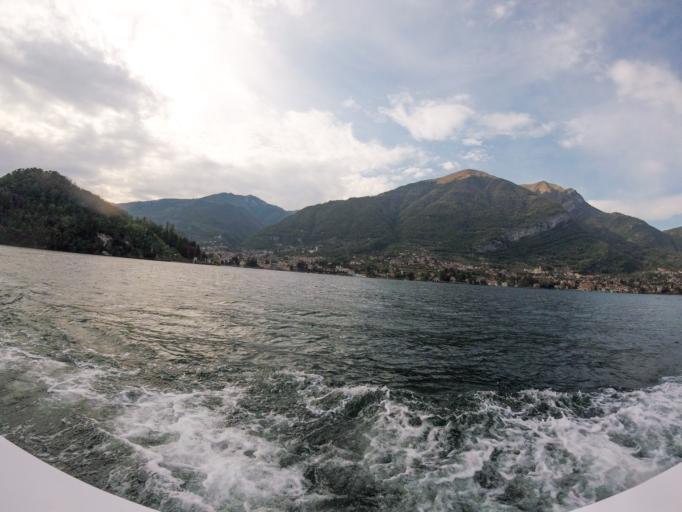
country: IT
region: Lombardy
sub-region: Provincia di Como
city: Mezzegra
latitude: 45.9689
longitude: 9.2084
